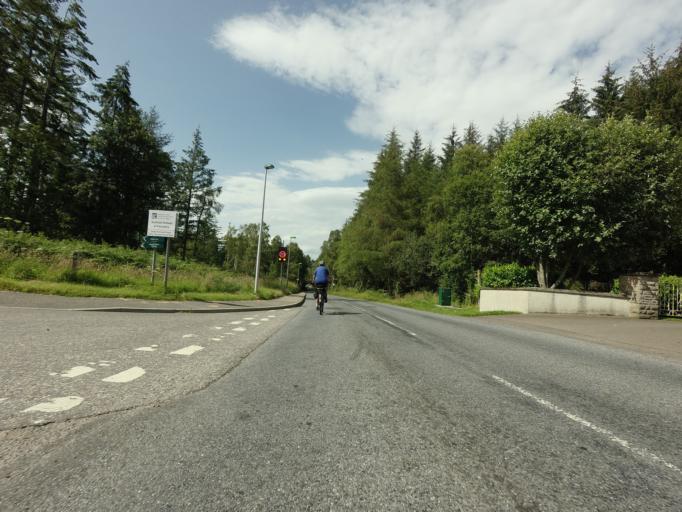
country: GB
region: Scotland
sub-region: Highland
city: Fortrose
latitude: 57.4897
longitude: -4.1053
